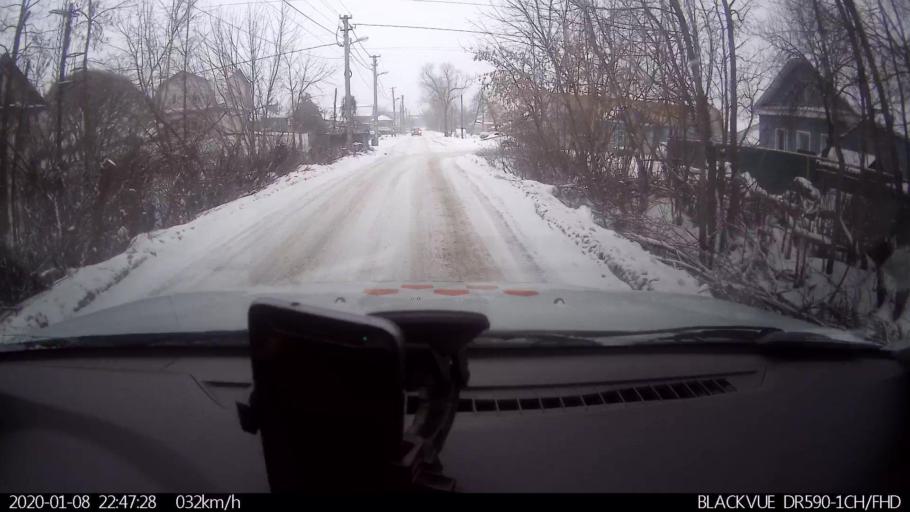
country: RU
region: Nizjnij Novgorod
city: Nizhniy Novgorod
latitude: 56.2922
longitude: 43.8935
